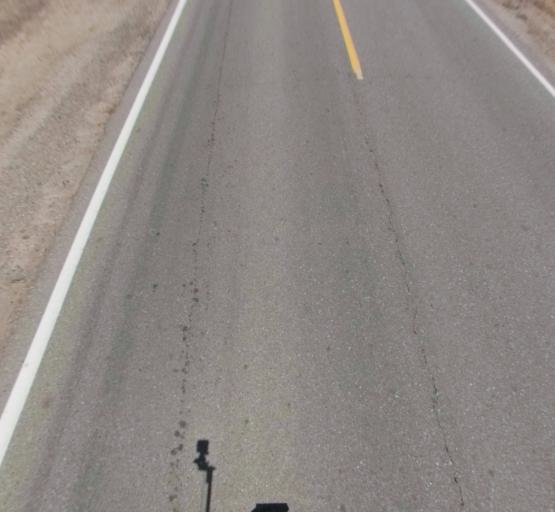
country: US
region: California
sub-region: Madera County
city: Fairmead
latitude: 37.0402
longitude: -120.2550
